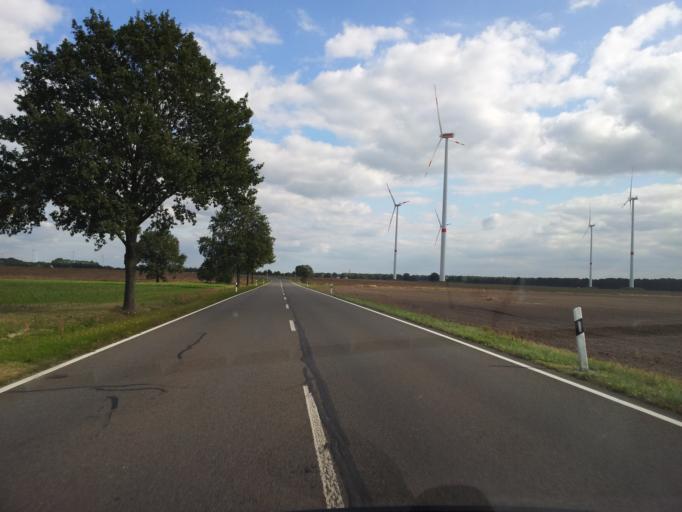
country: DE
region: Brandenburg
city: Sallgast
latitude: 51.6051
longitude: 13.8762
